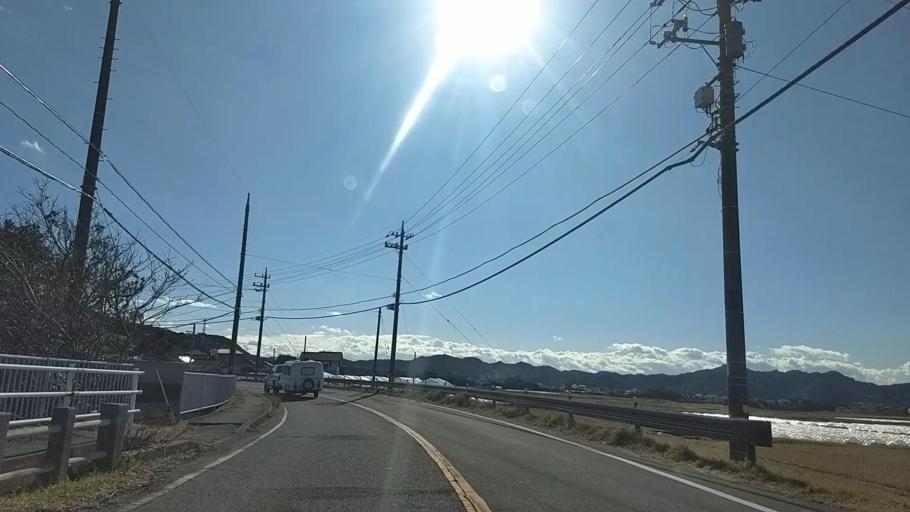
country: JP
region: Chiba
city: Tateyama
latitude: 34.9425
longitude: 139.8375
